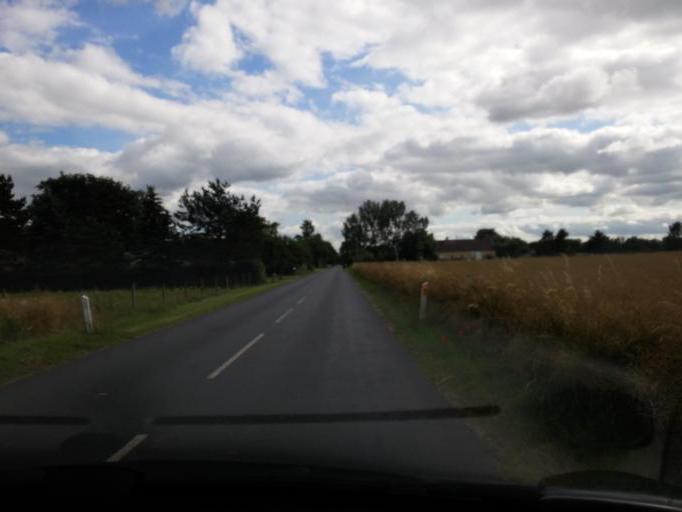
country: DK
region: South Denmark
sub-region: Kerteminde Kommune
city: Munkebo
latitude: 55.4364
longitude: 10.5407
